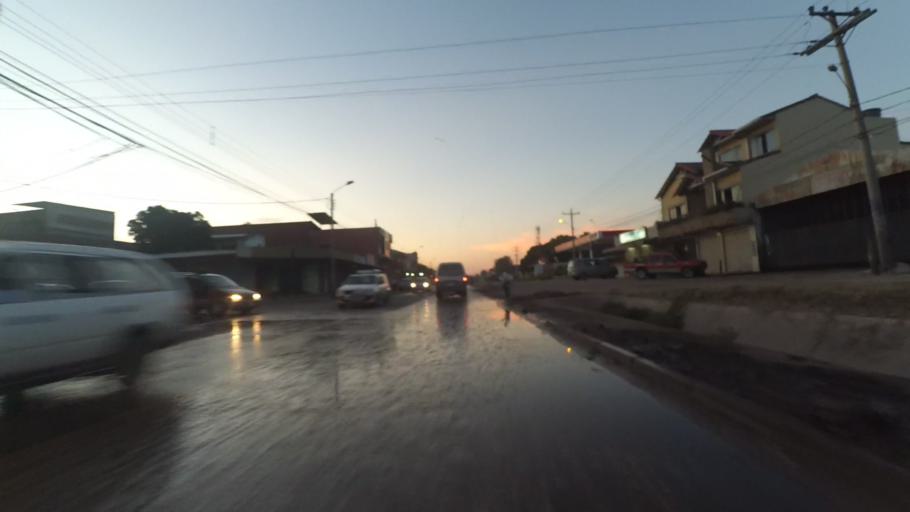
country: BO
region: Santa Cruz
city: Santa Cruz de la Sierra
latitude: -17.8194
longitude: -63.1376
